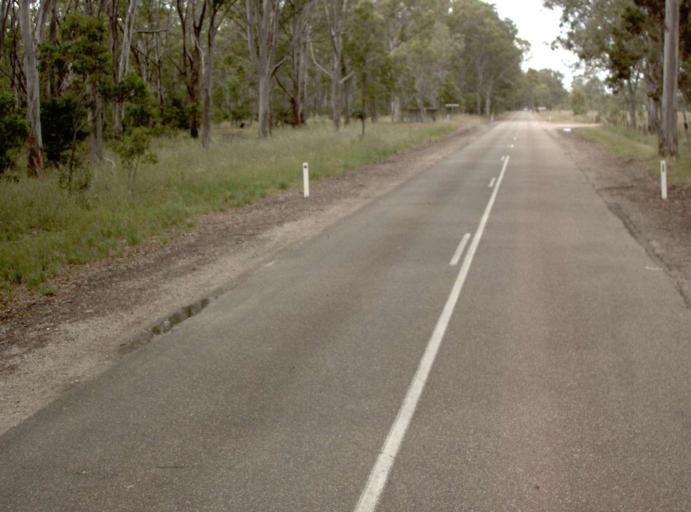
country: AU
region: Victoria
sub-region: Wellington
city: Sale
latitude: -37.8538
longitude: 147.0706
